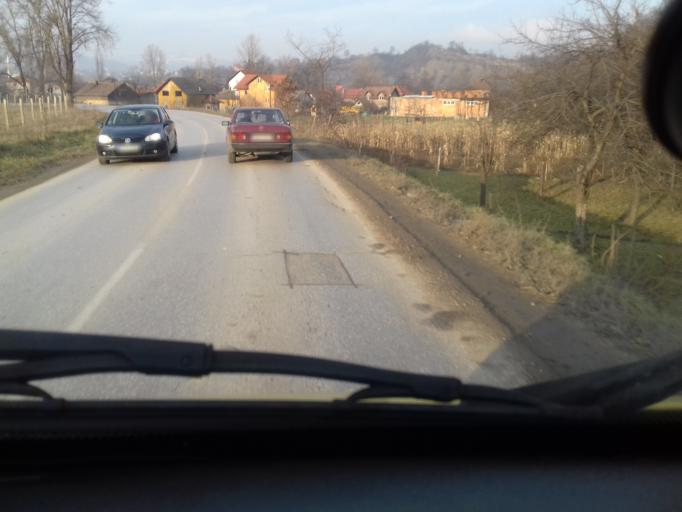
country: BA
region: Federation of Bosnia and Herzegovina
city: Kakanj
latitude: 44.1098
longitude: 18.1193
